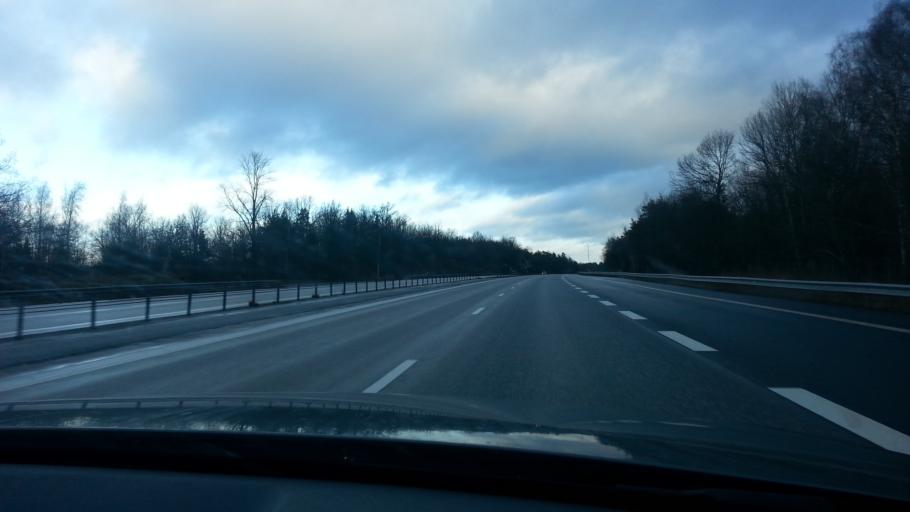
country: SE
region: OEstergoetland
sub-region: Odeshogs Kommun
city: OEdeshoeg
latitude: 58.1480
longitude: 14.5732
